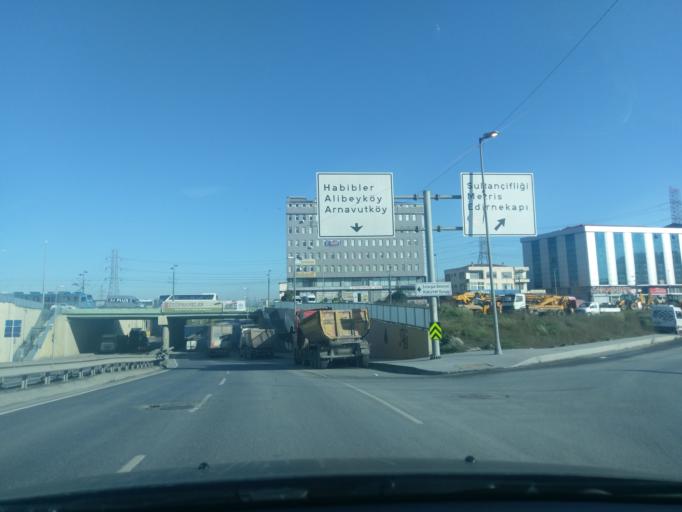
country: TR
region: Istanbul
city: Sultangazi
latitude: 41.1146
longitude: 28.8518
